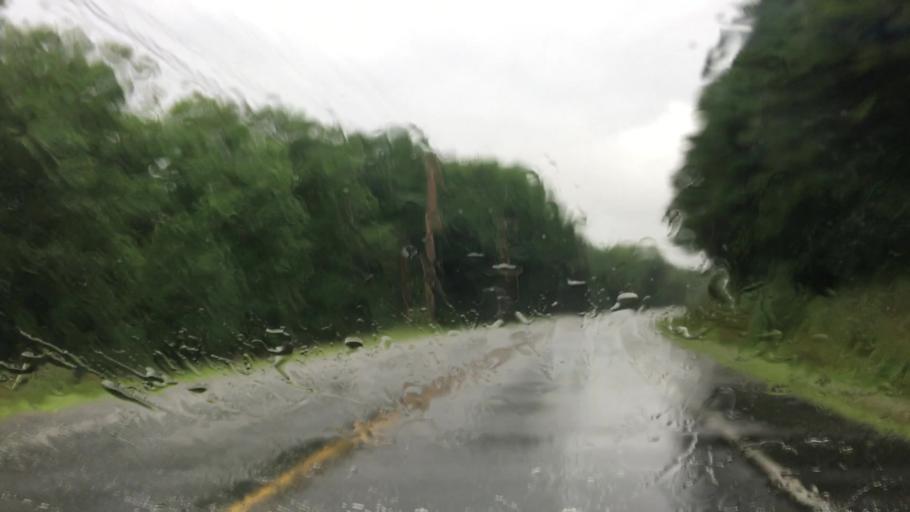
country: US
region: Maine
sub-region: Kennebec County
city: Pittston
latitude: 44.2189
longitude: -69.7629
